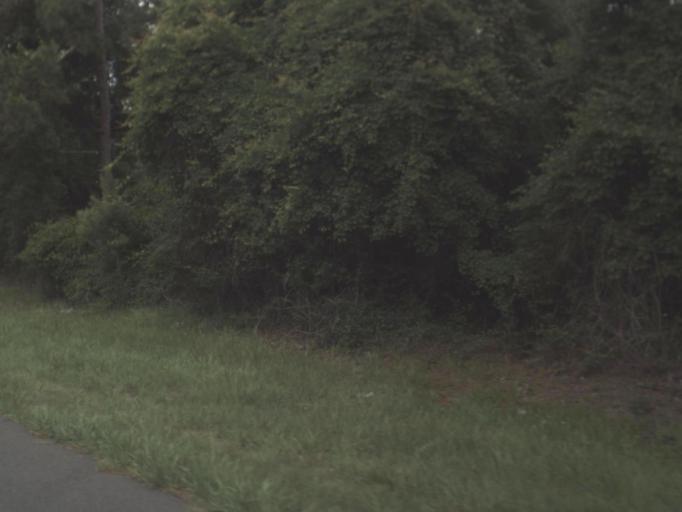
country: US
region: Florida
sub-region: Alachua County
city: Hawthorne
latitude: 29.5978
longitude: -82.0493
